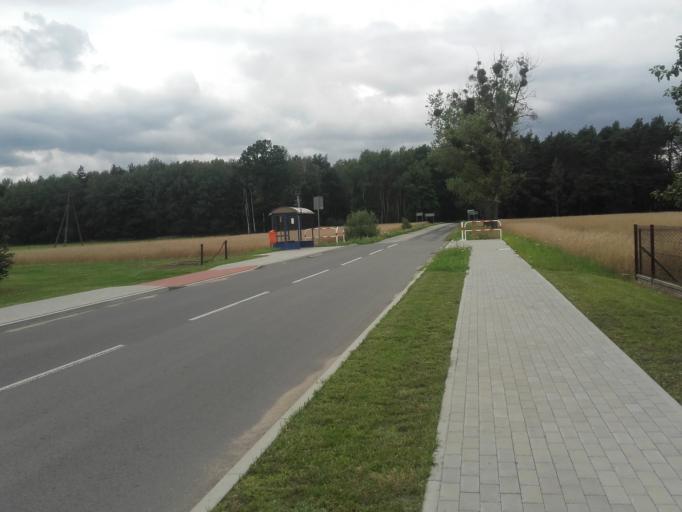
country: PL
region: Opole Voivodeship
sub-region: Powiat oleski
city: Olesno
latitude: 50.9197
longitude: 18.4831
